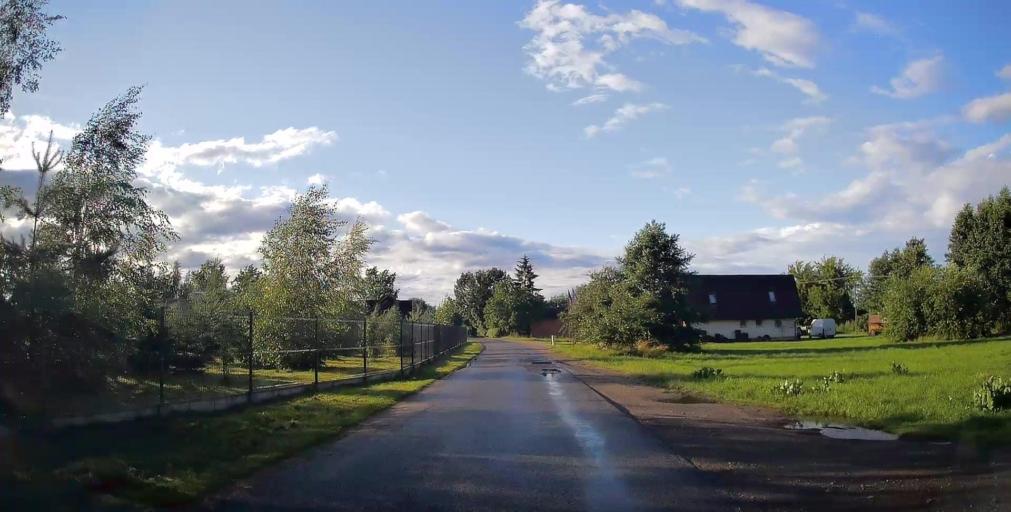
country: PL
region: Masovian Voivodeship
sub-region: Powiat grojecki
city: Goszczyn
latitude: 51.7580
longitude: 20.8810
